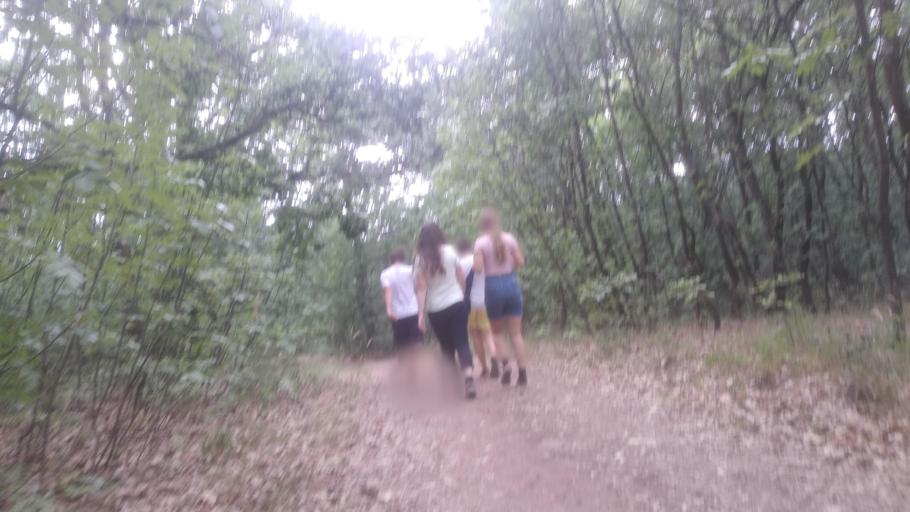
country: HU
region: Veszprem
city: Szentkiralyszabadja
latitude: 47.0037
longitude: 17.9745
